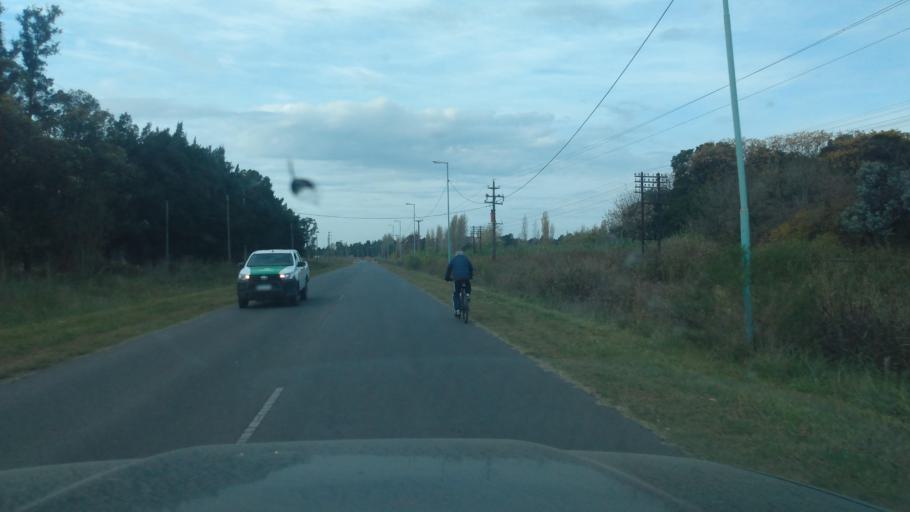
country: AR
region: Buenos Aires
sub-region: Partido de Lujan
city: Lujan
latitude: -34.5951
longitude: -59.1568
